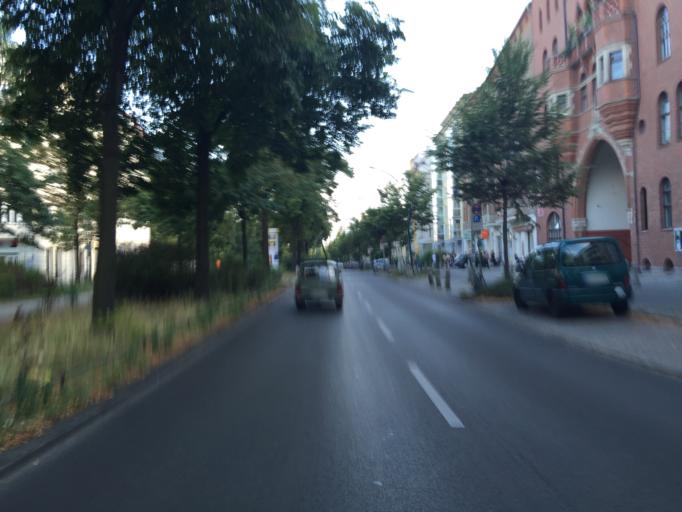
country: DE
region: Berlin
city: Berlin
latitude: 52.5365
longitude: 13.4122
